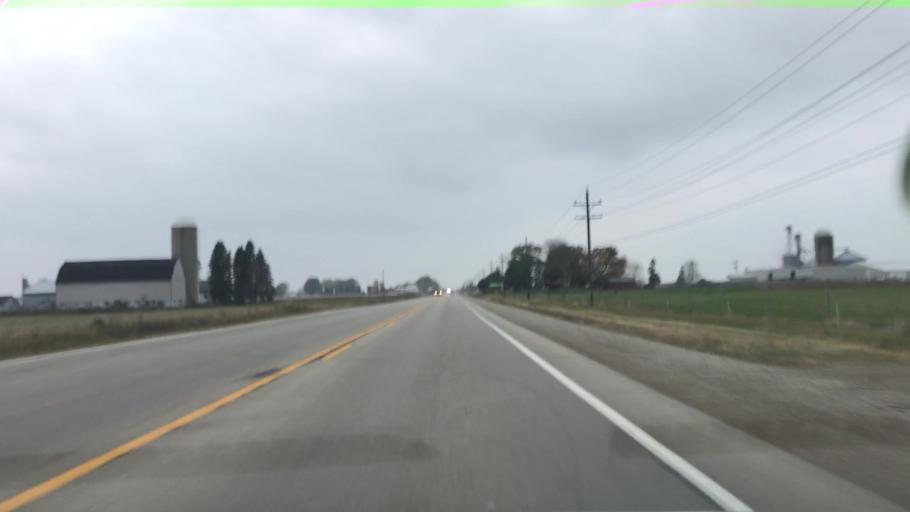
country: US
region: Wisconsin
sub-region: Outagamie County
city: Seymour
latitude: 44.5003
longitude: -88.2952
